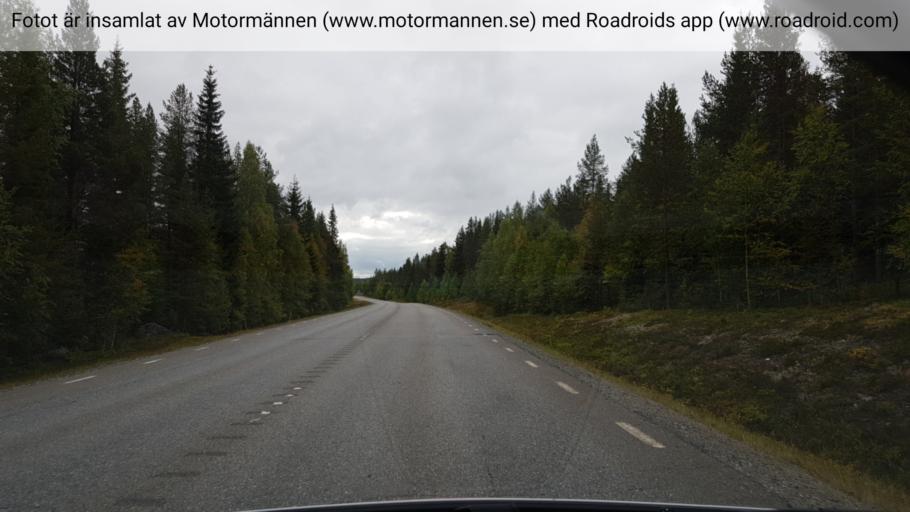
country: SE
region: Vaesterbotten
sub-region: Skelleftea Kommun
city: Boliden
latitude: 64.8887
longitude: 20.3790
